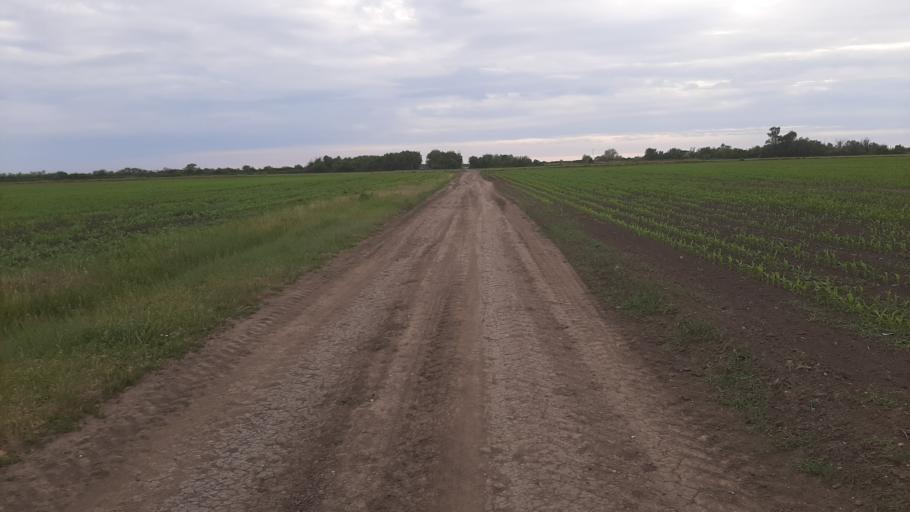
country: HU
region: Csongrad
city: Deszk
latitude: 46.1717
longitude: 20.2090
